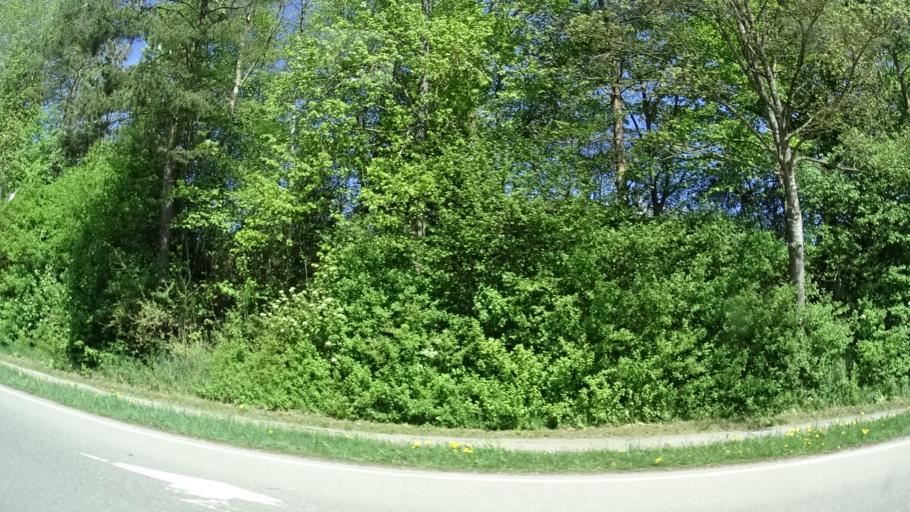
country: DE
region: Baden-Wuerttemberg
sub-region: Freiburg Region
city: Zimmern ob Rottweil
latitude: 48.1650
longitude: 8.6085
